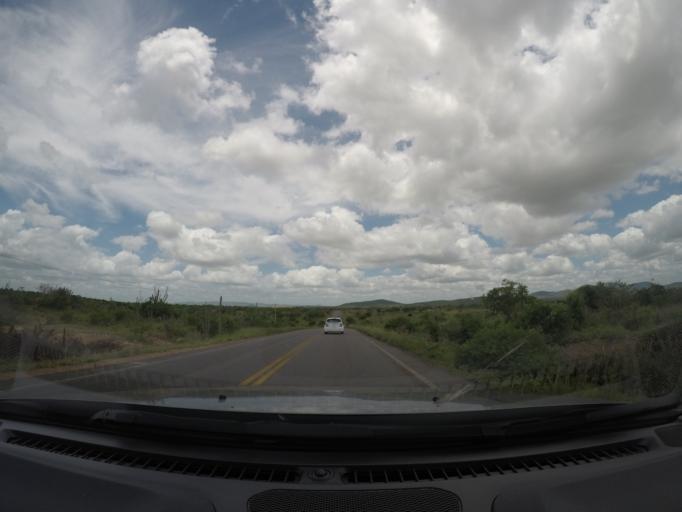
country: BR
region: Bahia
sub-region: Ipira
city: Ipira
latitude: -12.2796
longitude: -39.8597
